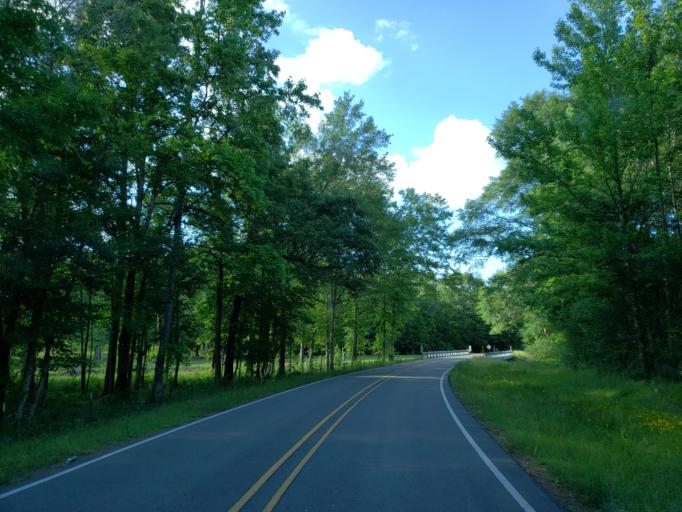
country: US
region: Mississippi
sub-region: Forrest County
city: Petal
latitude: 31.3182
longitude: -89.2120
